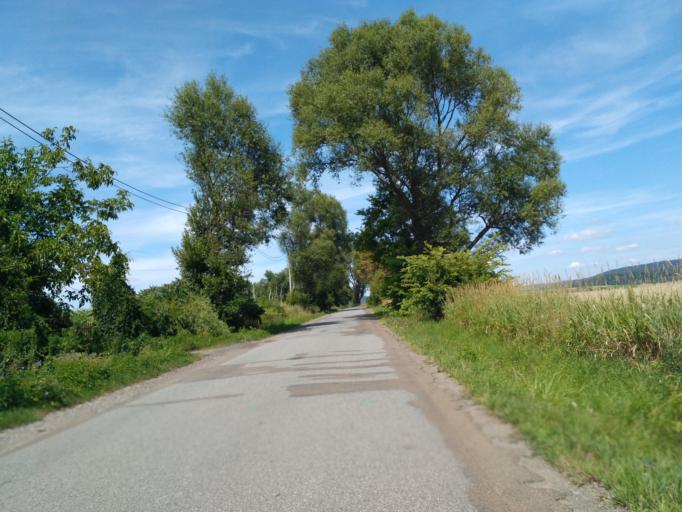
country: PL
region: Subcarpathian Voivodeship
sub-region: Powiat sanocki
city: Strachocina
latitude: 49.5701
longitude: 22.1212
